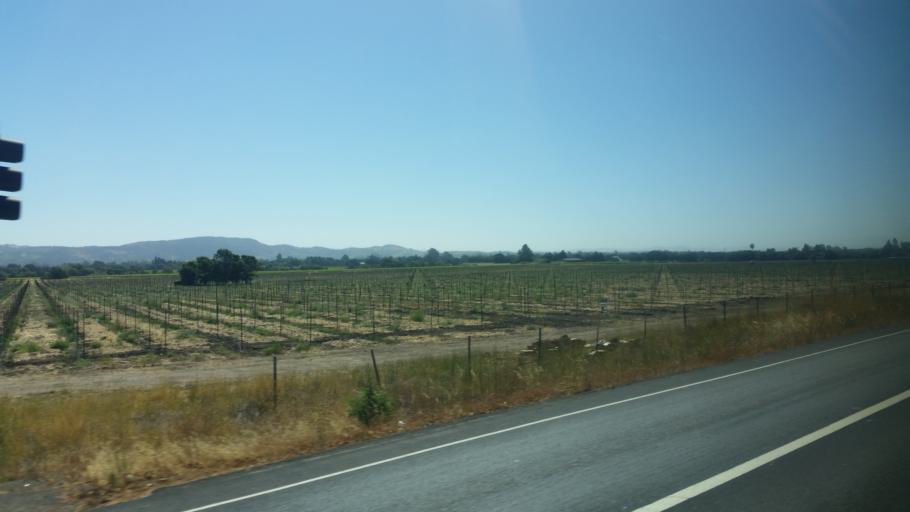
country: US
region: California
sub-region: Sonoma County
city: Temelec
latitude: 38.2656
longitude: -122.4878
